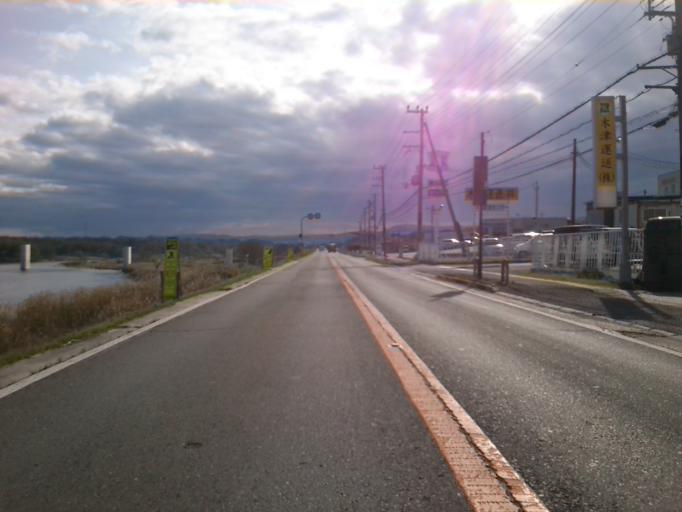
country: JP
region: Nara
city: Nara-shi
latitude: 34.7507
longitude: 135.8337
